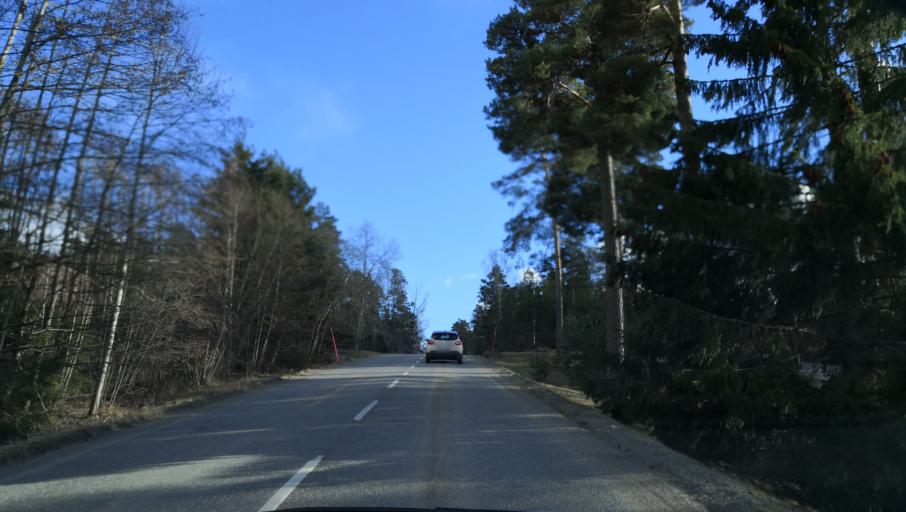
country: SE
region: Stockholm
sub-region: Varmdo Kommun
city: Mortnas
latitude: 59.2853
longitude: 18.4542
